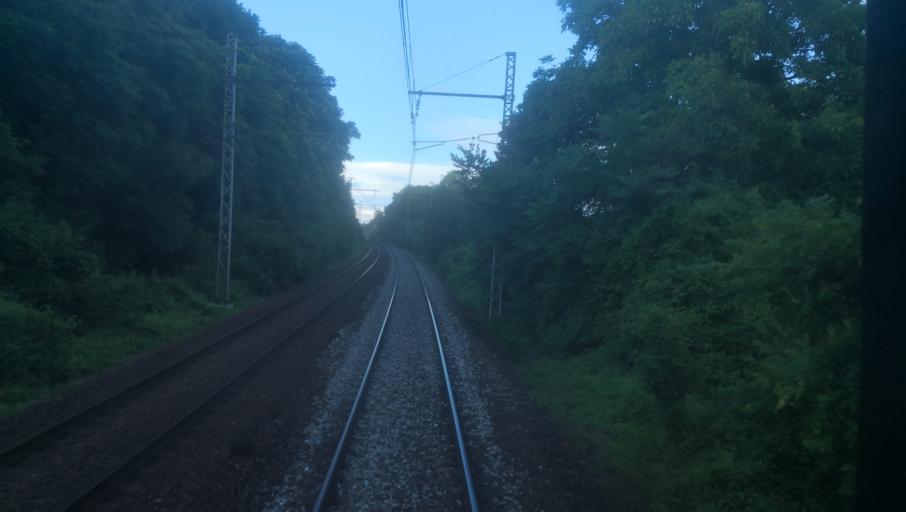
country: FR
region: Centre
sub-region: Departement de l'Indre
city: Issoudun
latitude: 46.9680
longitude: 2.0009
